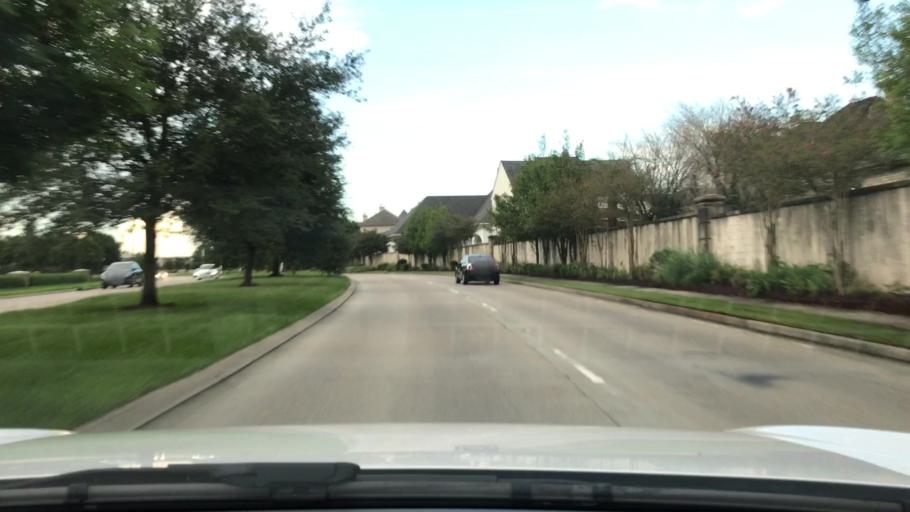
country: US
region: Louisiana
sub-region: East Baton Rouge Parish
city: Westminster
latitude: 30.4254
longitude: -91.1218
